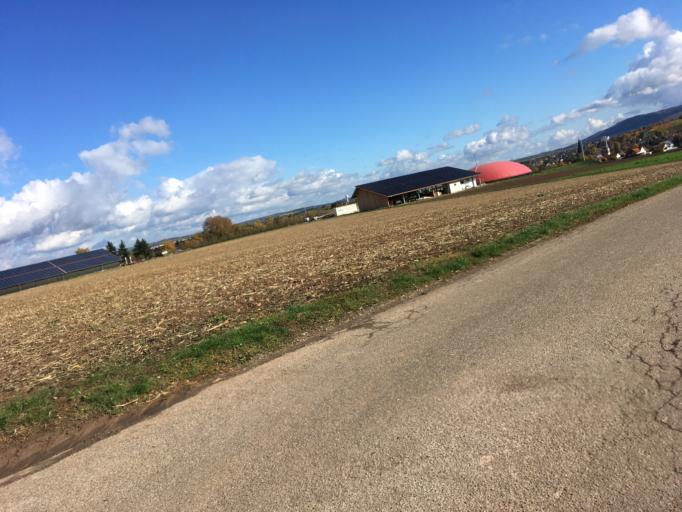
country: DE
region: Baden-Wuerttemberg
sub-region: Regierungsbezirk Stuttgart
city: Pfedelbach
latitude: 49.1757
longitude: 9.4917
